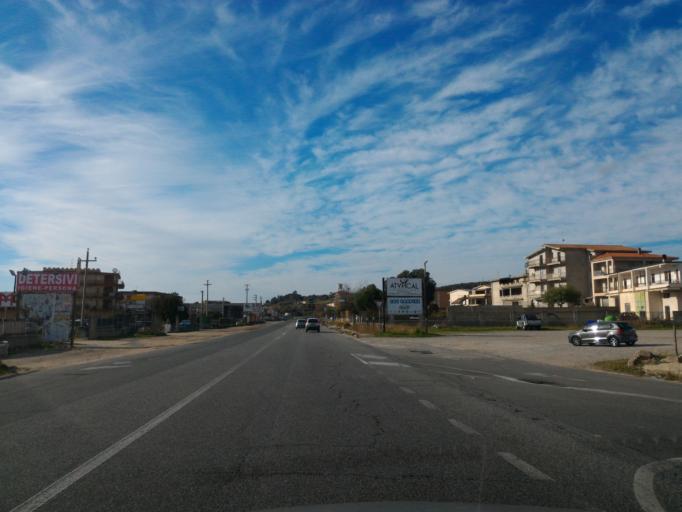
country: IT
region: Calabria
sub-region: Provincia di Catanzaro
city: Sellia Marina
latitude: 38.8947
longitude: 16.7269
